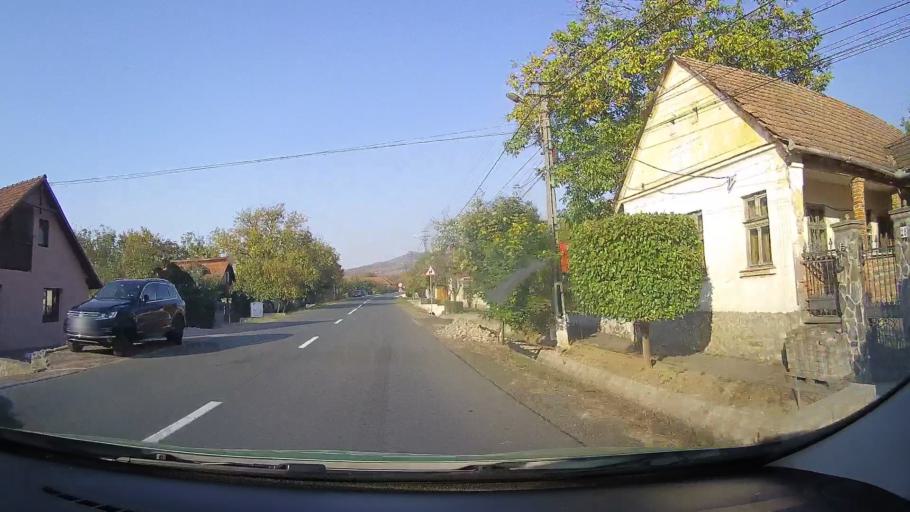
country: RO
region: Arad
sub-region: Comuna Ghioroc
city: Ghioroc
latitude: 46.1338
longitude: 21.6029
